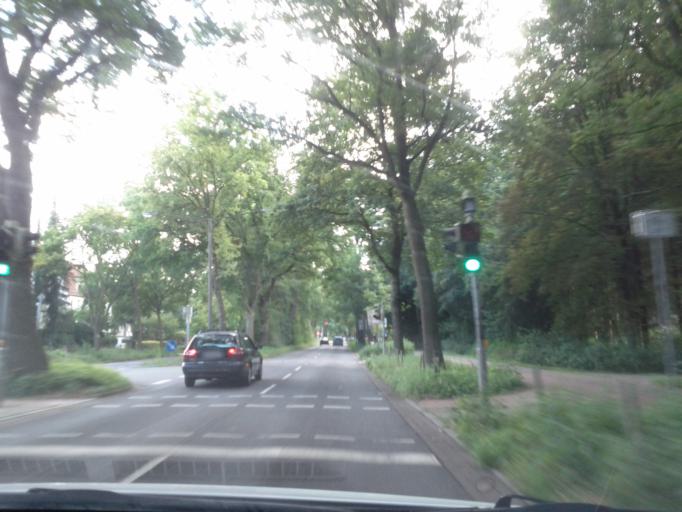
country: DE
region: Bremen
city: Bremen
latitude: 53.0948
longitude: 8.8335
